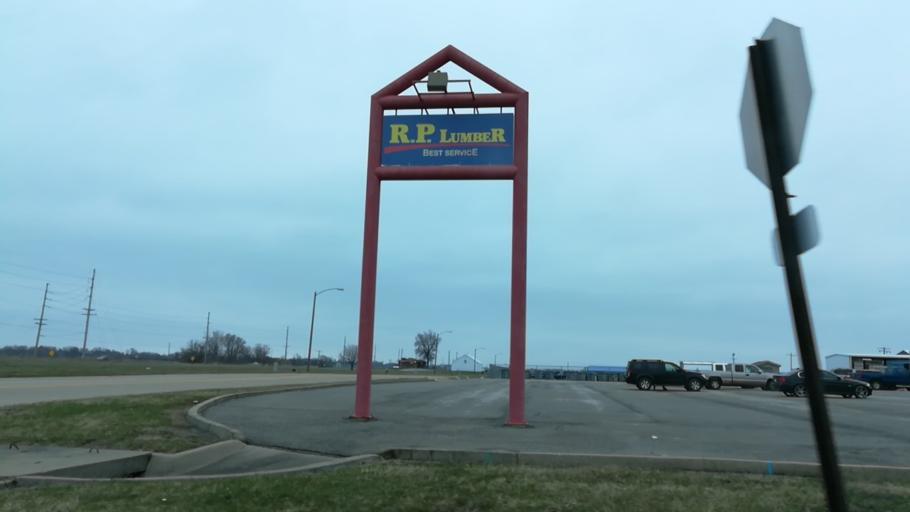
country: US
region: Illinois
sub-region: Madison County
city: Troy
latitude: 38.7163
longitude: -89.9100
